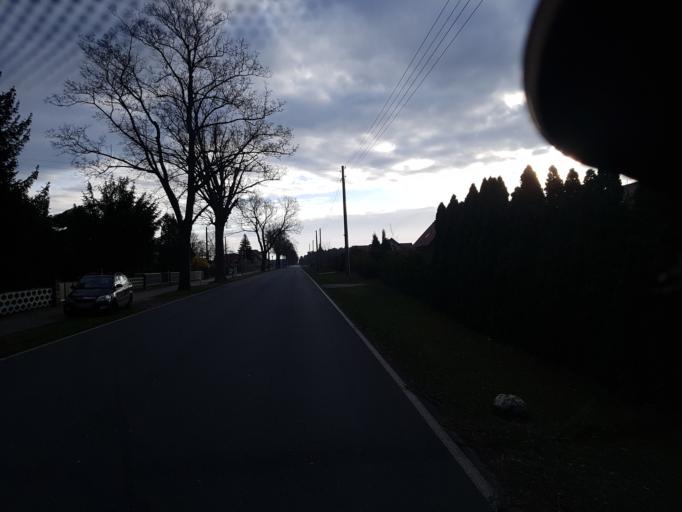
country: DE
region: Brandenburg
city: Schlepzig
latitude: 51.9870
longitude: 13.9810
